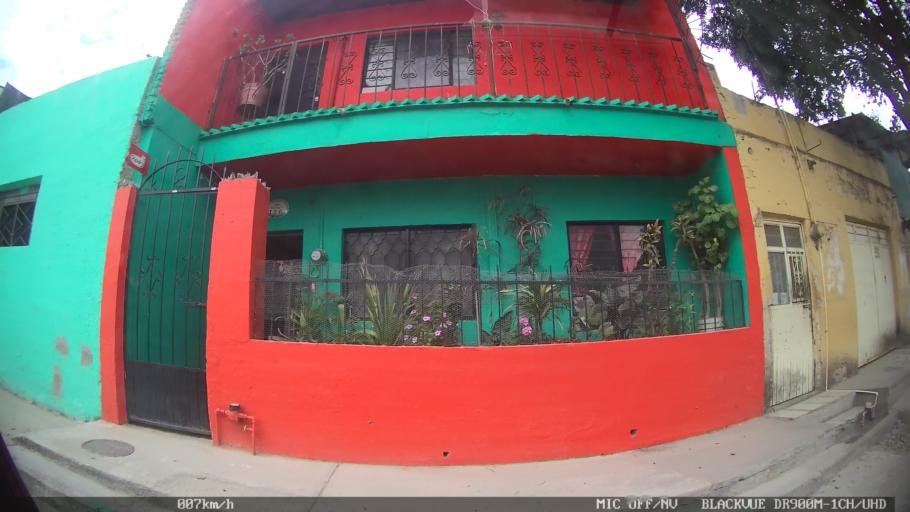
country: MX
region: Jalisco
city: Tonala
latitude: 20.6505
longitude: -103.2580
